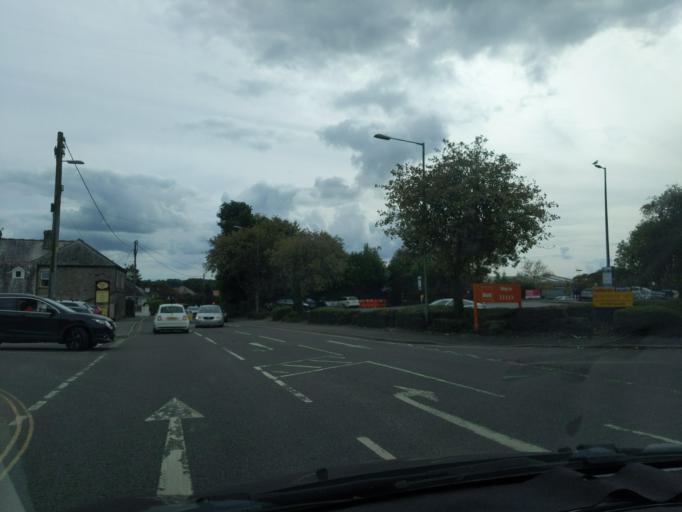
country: GB
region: England
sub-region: Cornwall
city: St Austell
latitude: 50.3336
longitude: -4.7934
